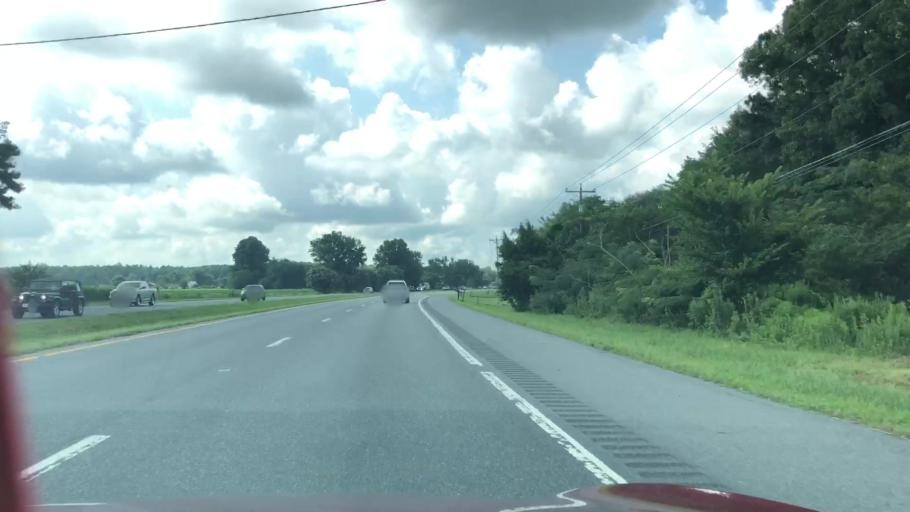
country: US
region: Virginia
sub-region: Accomack County
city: Wattsville
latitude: 37.9594
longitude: -75.5336
